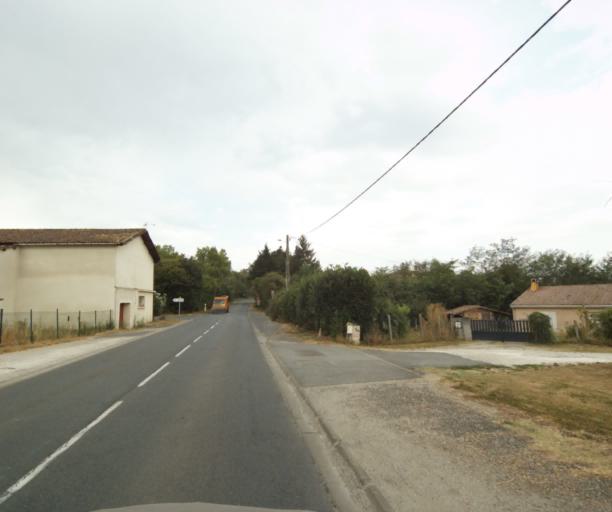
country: FR
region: Aquitaine
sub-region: Departement de la Gironde
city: La Sauve
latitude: 44.7509
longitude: -0.3329
